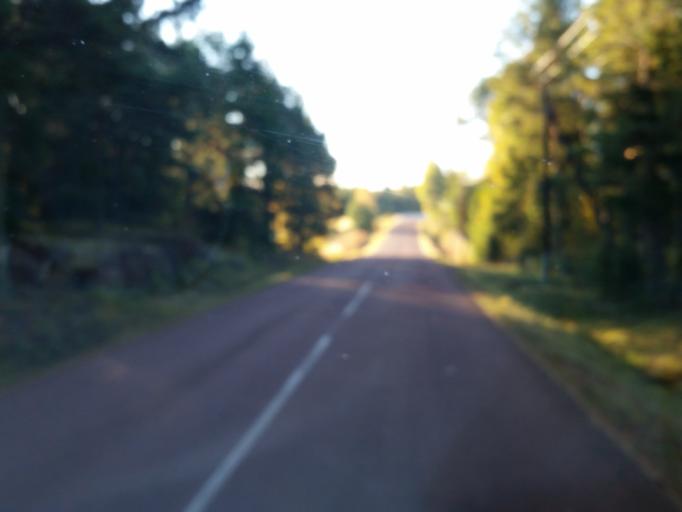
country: AX
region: Alands skaergard
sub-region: Vardoe
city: Vardoe
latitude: 60.2970
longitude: 20.3843
